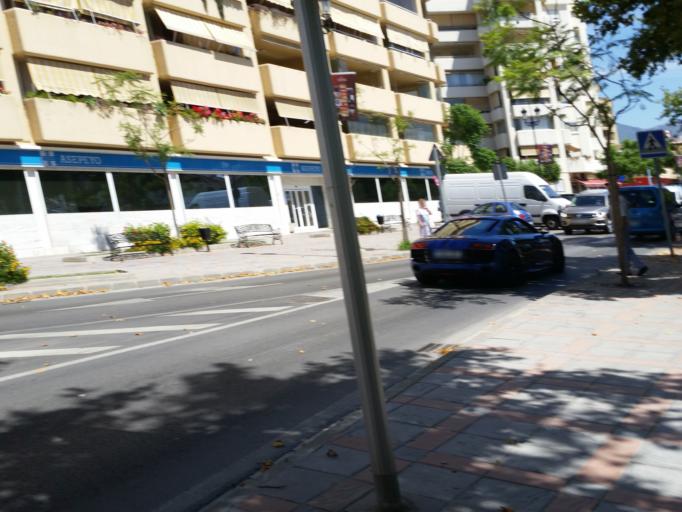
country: ES
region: Andalusia
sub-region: Provincia de Malaga
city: Fuengirola
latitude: 36.5311
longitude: -4.6273
